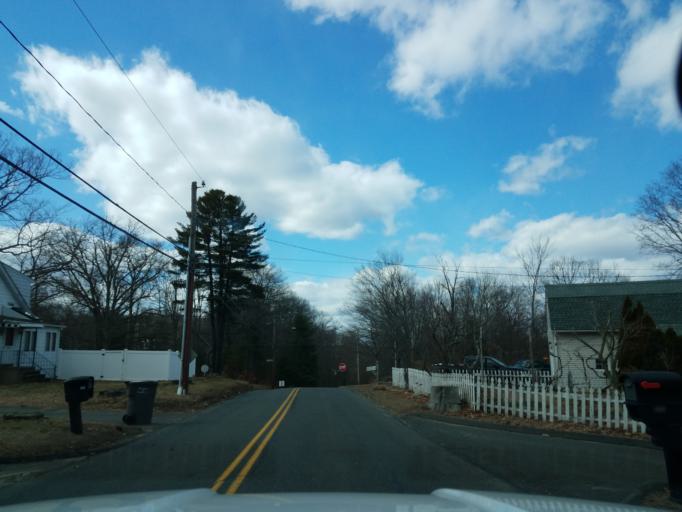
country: US
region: Connecticut
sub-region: New Haven County
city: Naugatuck
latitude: 41.5018
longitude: -73.0200
